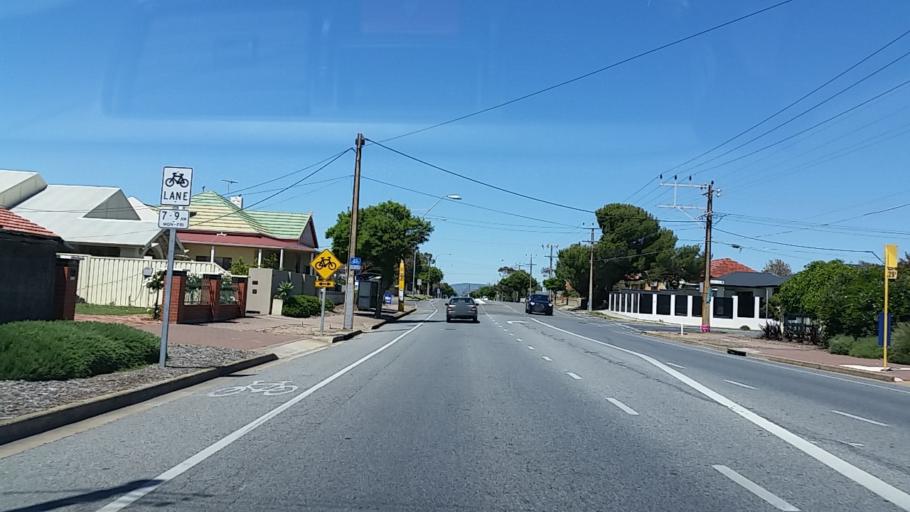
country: AU
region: South Australia
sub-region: Charles Sturt
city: Grange
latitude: -34.9072
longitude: 138.4957
